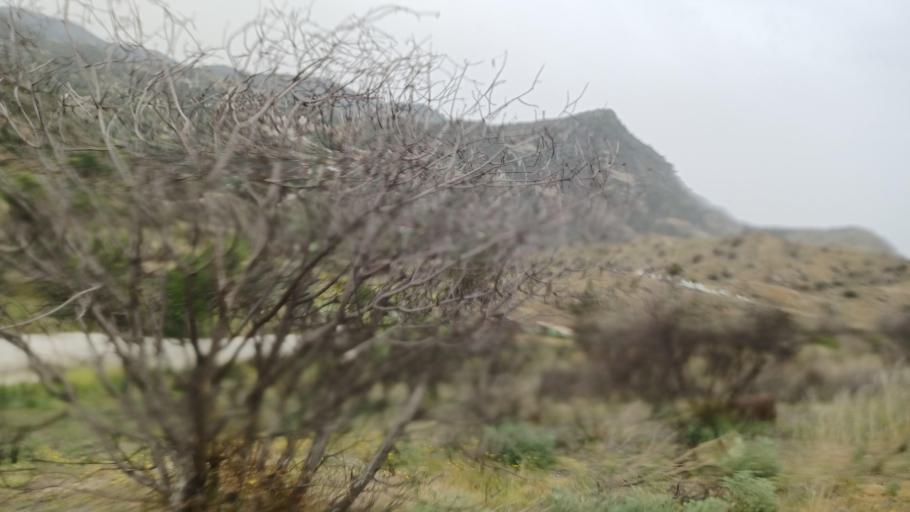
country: CY
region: Limassol
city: Parekklisha
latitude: 34.8388
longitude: 33.1222
